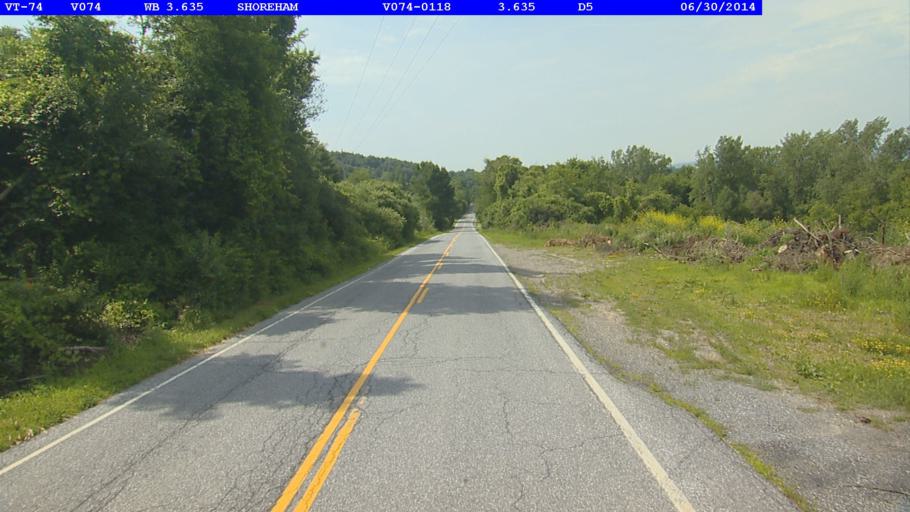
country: US
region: New York
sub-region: Essex County
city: Ticonderoga
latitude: 43.8842
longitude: -73.3335
